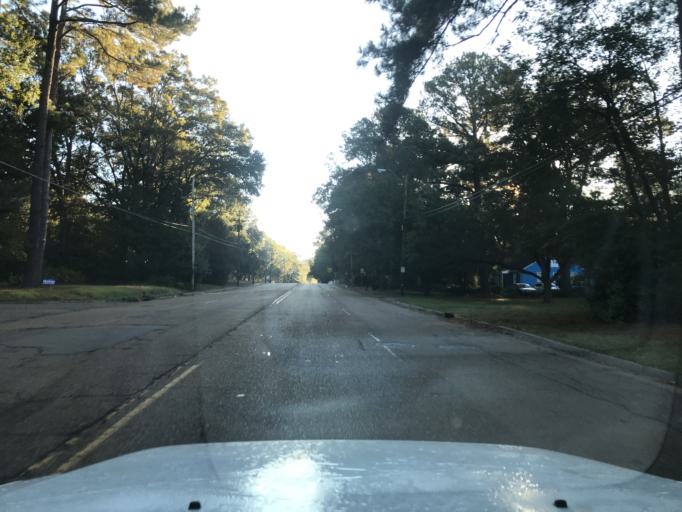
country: US
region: Mississippi
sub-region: Rankin County
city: Flowood
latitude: 32.3502
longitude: -90.1680
